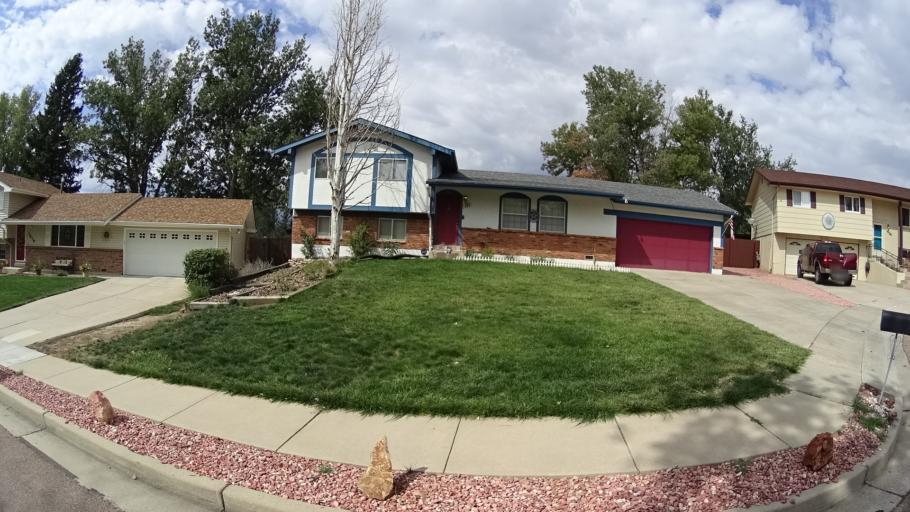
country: US
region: Colorado
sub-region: El Paso County
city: Cimarron Hills
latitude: 38.8560
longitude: -104.7374
